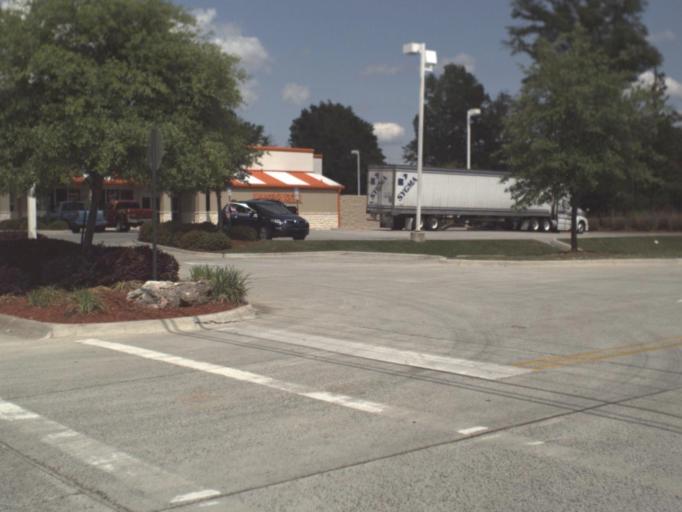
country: US
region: Florida
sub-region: Escambia County
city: Century
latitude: 30.9799
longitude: -87.2587
